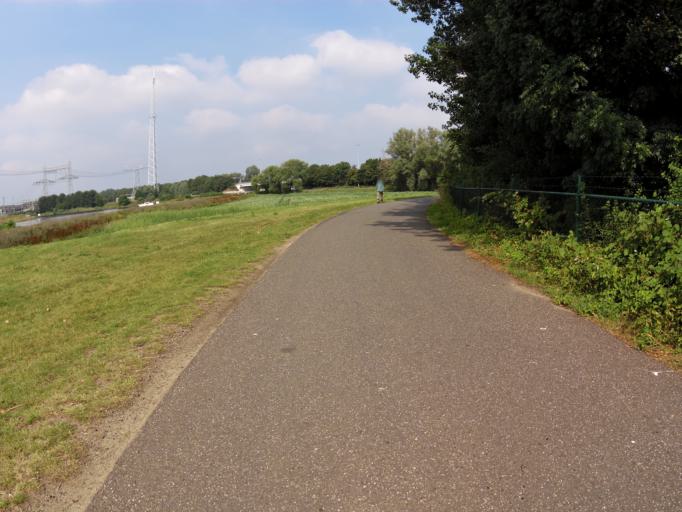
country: NL
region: North Brabant
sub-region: Gemeente 's-Hertogenbosch
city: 's-Hertogenbosch
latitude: 51.7139
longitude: 5.2807
